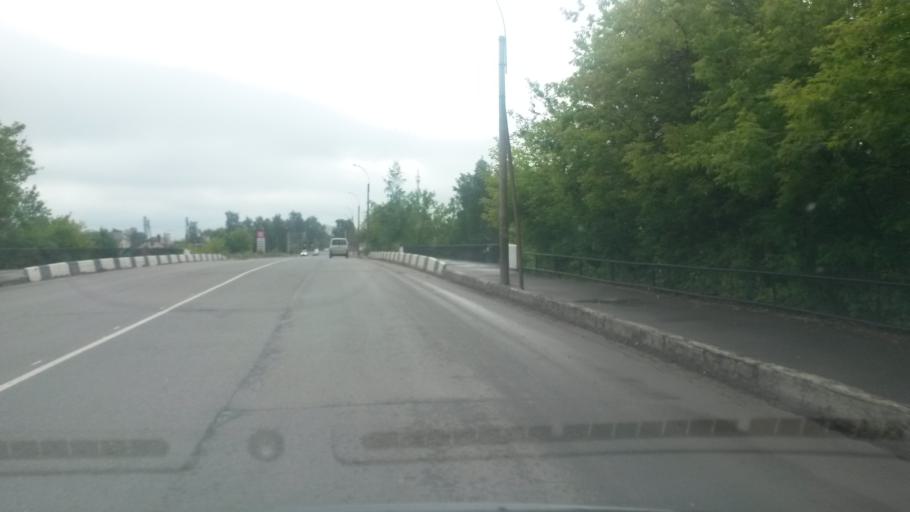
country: RU
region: Ivanovo
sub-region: Gorod Ivanovo
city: Ivanovo
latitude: 57.0177
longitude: 40.9248
